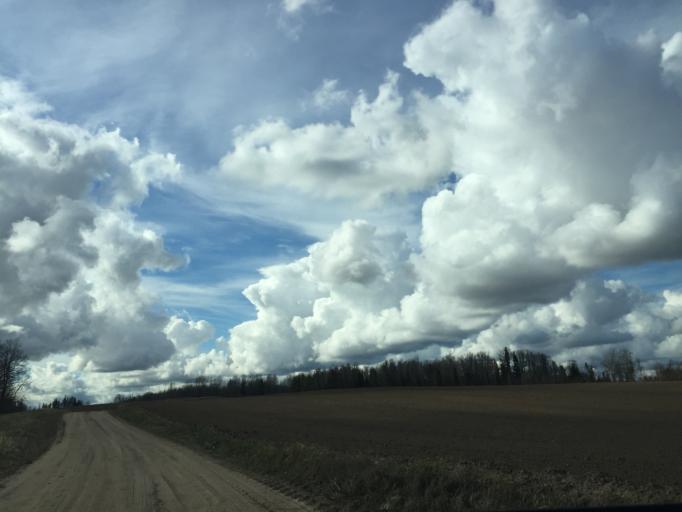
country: LV
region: Burtnieki
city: Matisi
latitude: 57.6167
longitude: 25.0004
